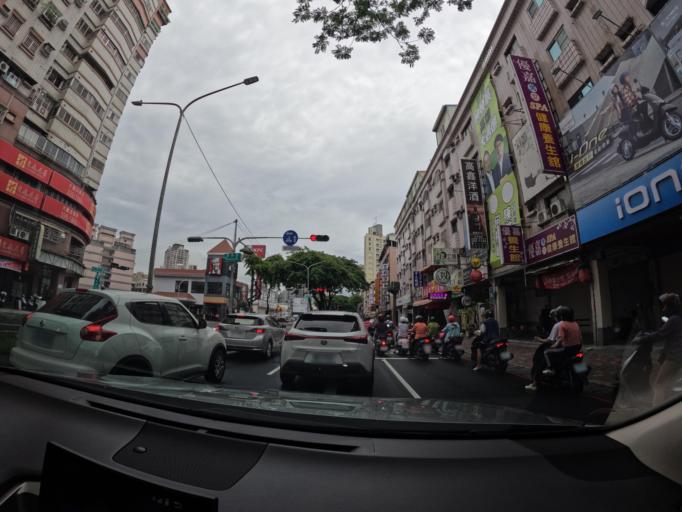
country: TW
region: Kaohsiung
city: Kaohsiung
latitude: 22.6449
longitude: 120.3259
